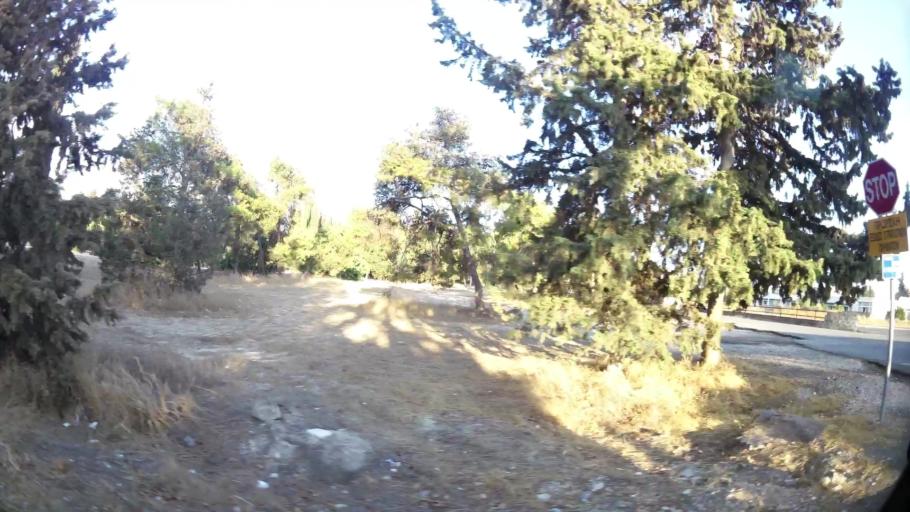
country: CY
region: Larnaka
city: Larnaca
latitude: 34.9241
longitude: 33.6069
